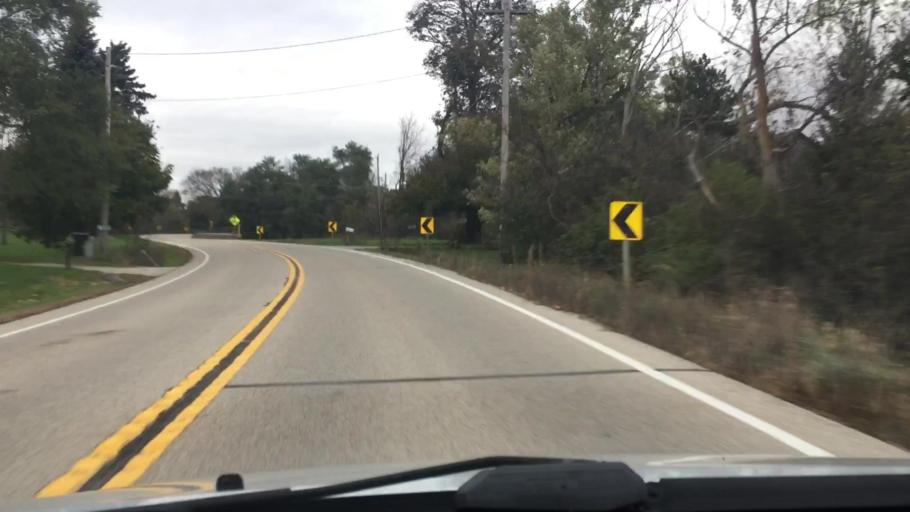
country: US
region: Wisconsin
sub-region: Waukesha County
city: Eagle
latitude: 42.8939
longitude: -88.4737
